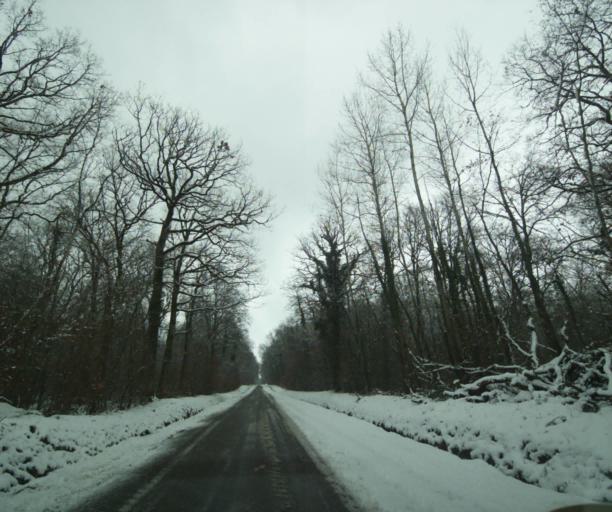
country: FR
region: Champagne-Ardenne
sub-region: Departement de la Haute-Marne
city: Laneuville-a-Remy
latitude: 48.3940
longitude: 4.8673
